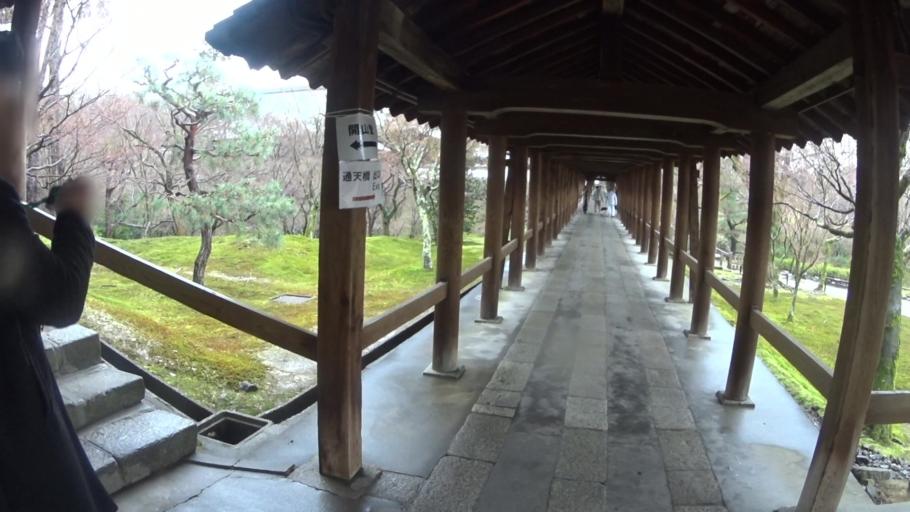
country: JP
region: Kyoto
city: Kyoto
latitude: 34.9776
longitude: 135.7740
